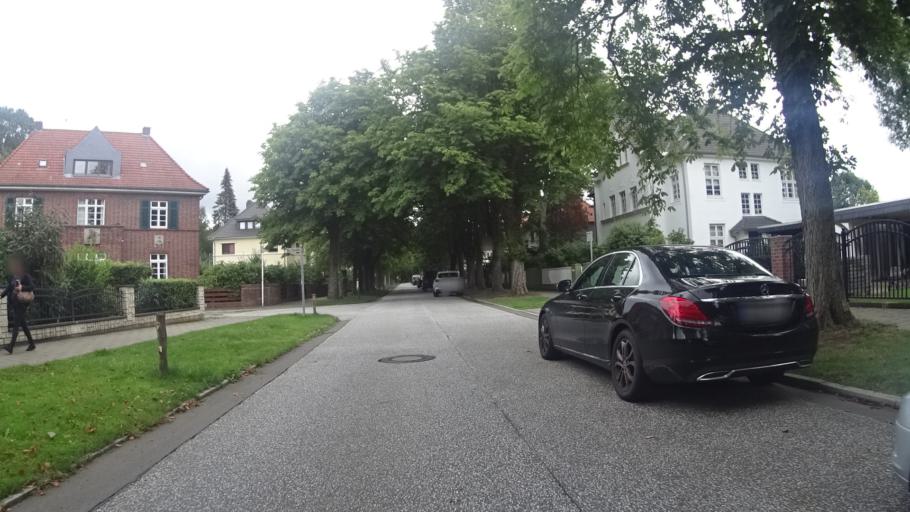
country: DE
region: Bremen
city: Bremerhaven
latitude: 53.5357
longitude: 8.6022
